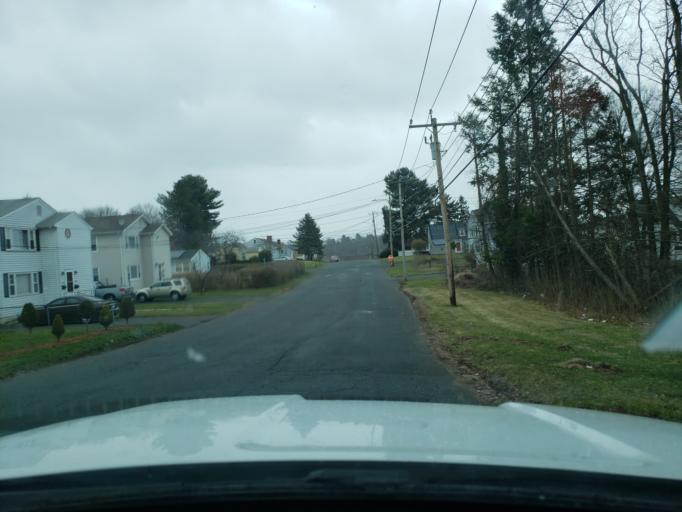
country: US
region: Connecticut
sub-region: Hartford County
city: New Britain
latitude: 41.6741
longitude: -72.7573
